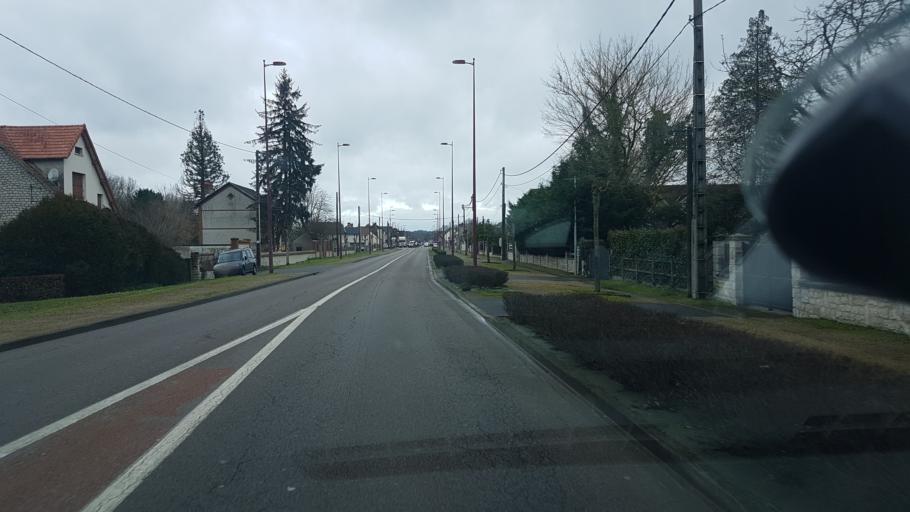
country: FR
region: Centre
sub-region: Departement du Loiret
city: Dordives
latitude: 48.1420
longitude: 2.7640
